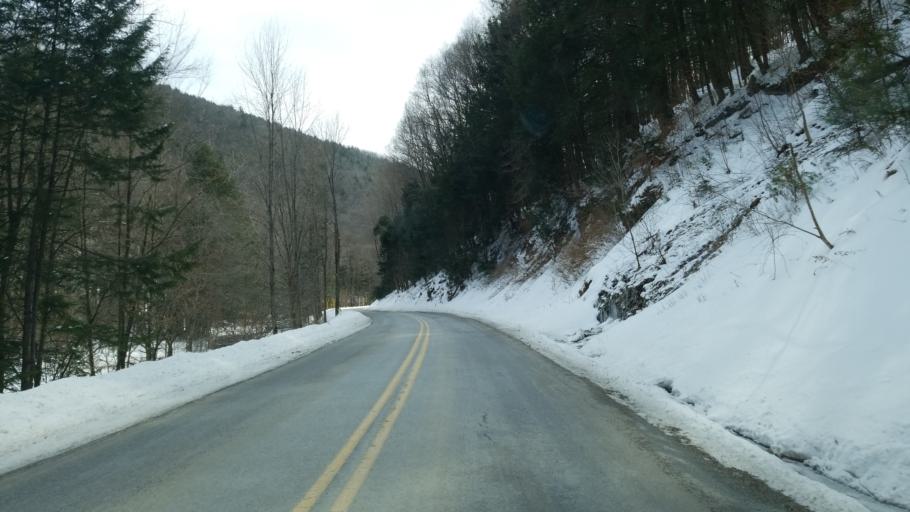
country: US
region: Pennsylvania
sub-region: Clearfield County
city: Shiloh
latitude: 41.2624
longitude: -78.1539
